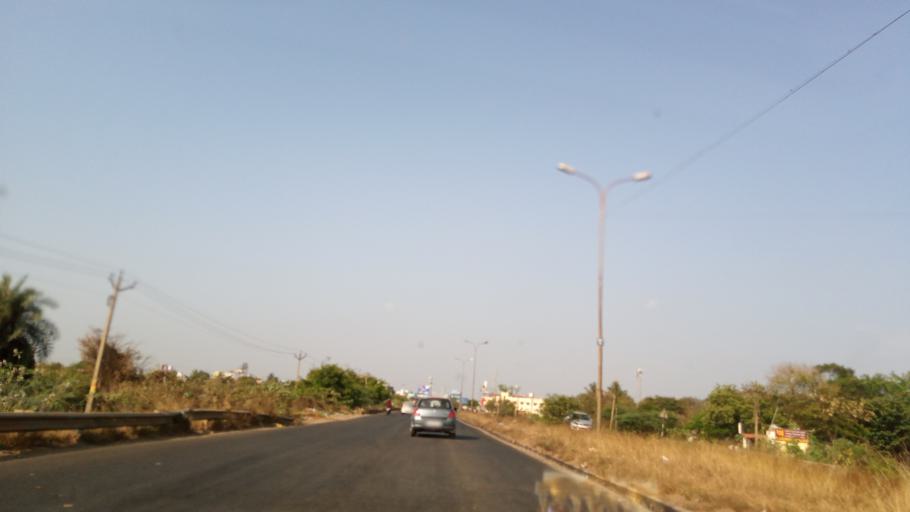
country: IN
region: Tamil Nadu
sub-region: Kancheepuram
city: Sriperumbudur
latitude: 13.0127
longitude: 80.0003
